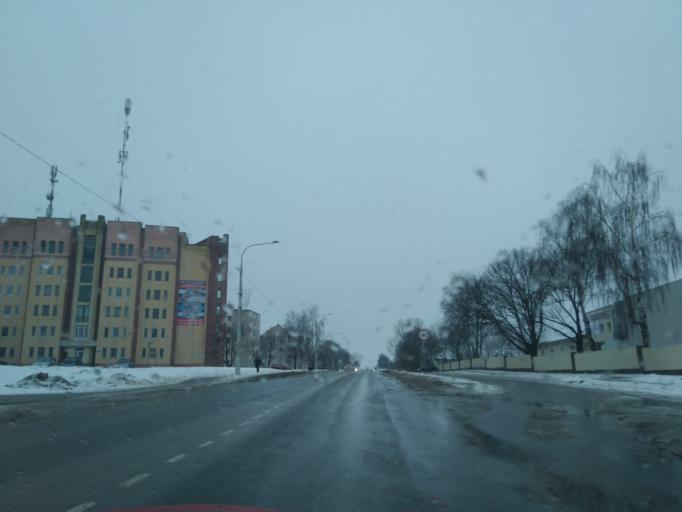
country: BY
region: Minsk
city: Nyasvizh
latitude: 53.2294
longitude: 26.6605
